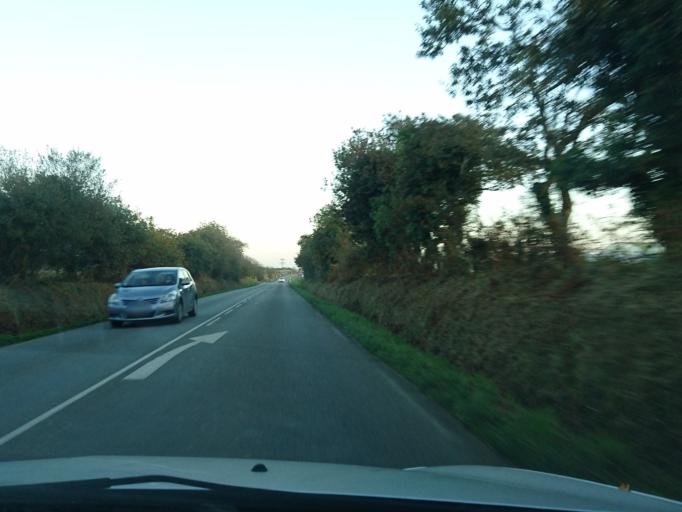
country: FR
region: Brittany
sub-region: Departement du Finistere
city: Lanrivoare
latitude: 48.4575
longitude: -4.6291
